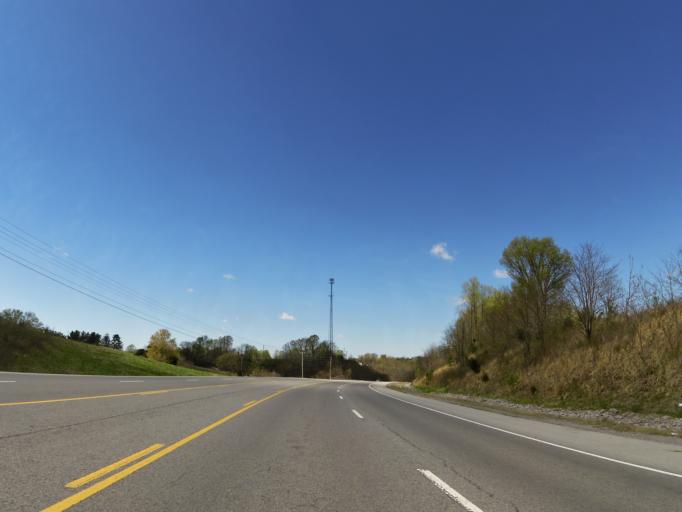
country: US
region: Tennessee
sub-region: DeKalb County
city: Smithville
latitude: 35.9929
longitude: -85.8883
